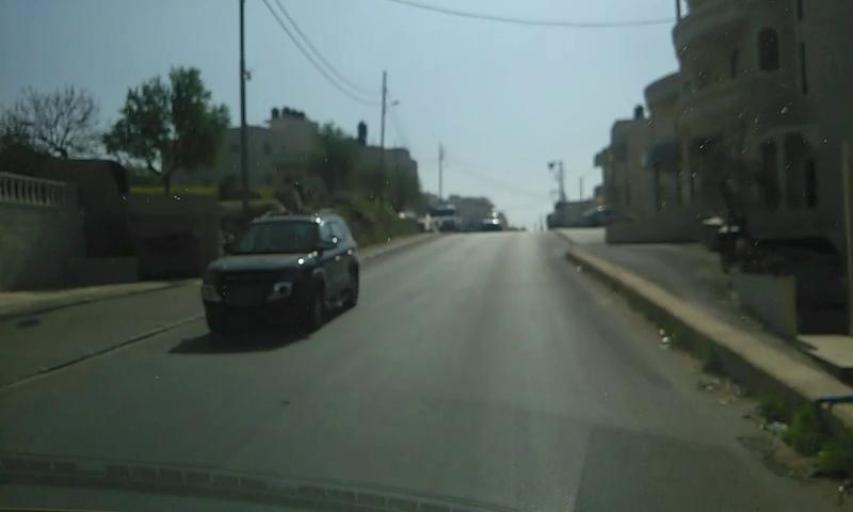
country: PS
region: West Bank
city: Dayr Jarir
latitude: 31.9694
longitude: 35.2886
